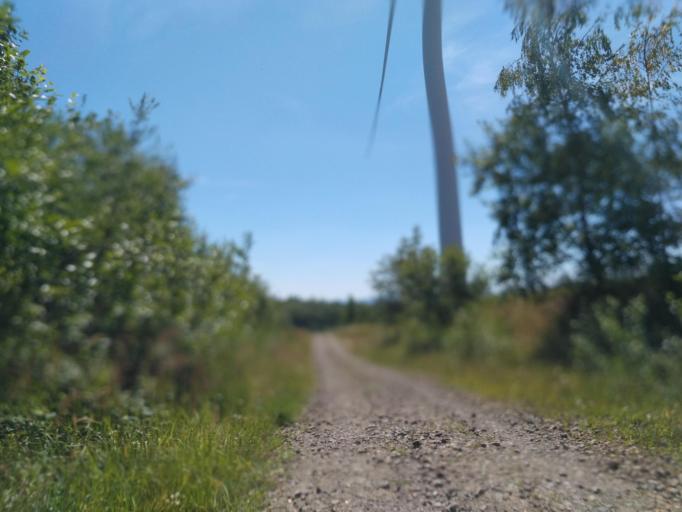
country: PL
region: Subcarpathian Voivodeship
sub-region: Powiat sanocki
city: Bukowsko
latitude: 49.5057
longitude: 22.0571
